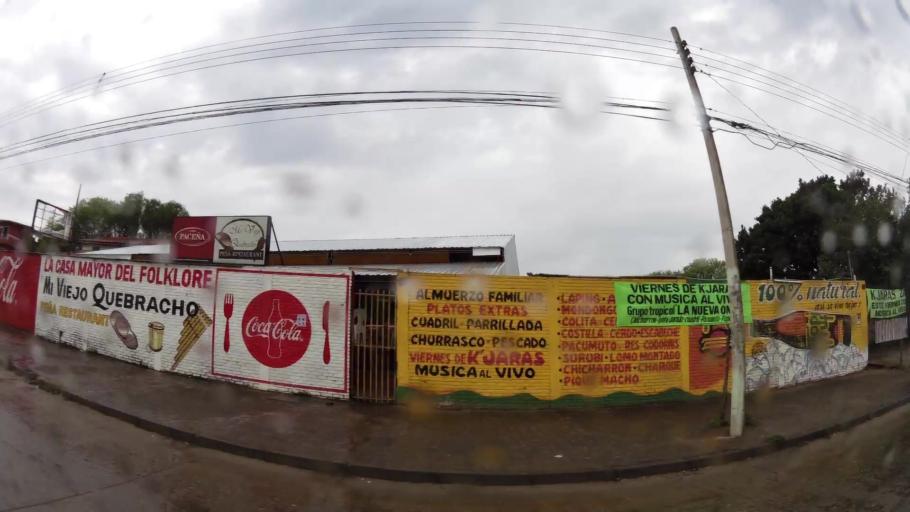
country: BO
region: Santa Cruz
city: Santa Cruz de la Sierra
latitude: -17.8075
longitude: -63.1519
